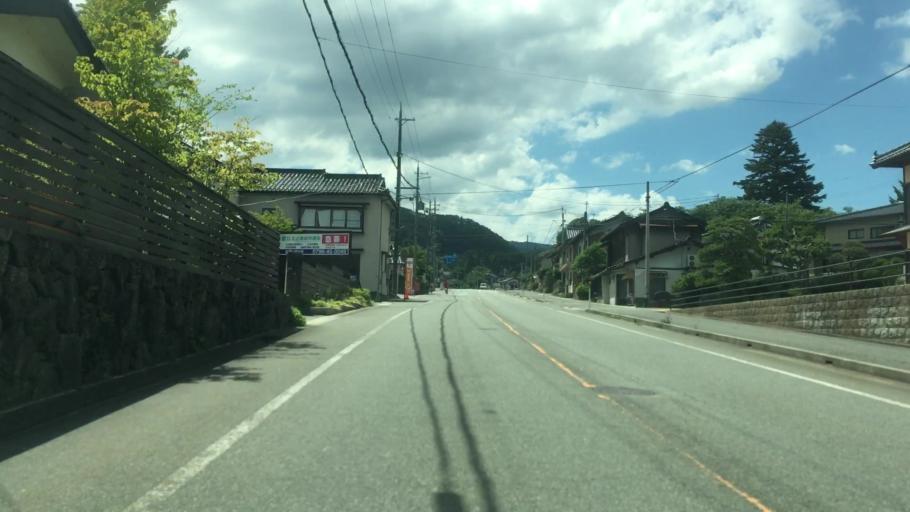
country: JP
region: Hyogo
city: Toyooka
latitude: 35.4867
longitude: 134.6976
